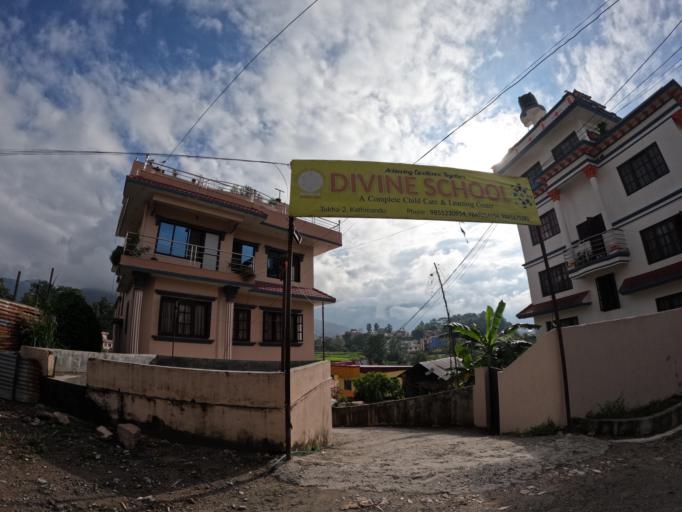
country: NP
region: Central Region
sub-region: Bagmati Zone
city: Kathmandu
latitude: 27.7682
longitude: 85.3311
